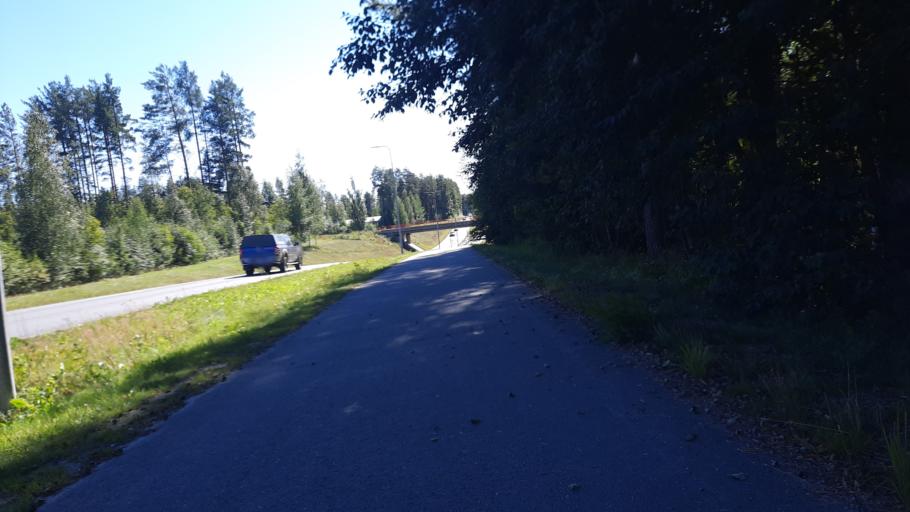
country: FI
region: North Karelia
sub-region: Joensuu
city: Joensuu
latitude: 62.6283
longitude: 29.7352
